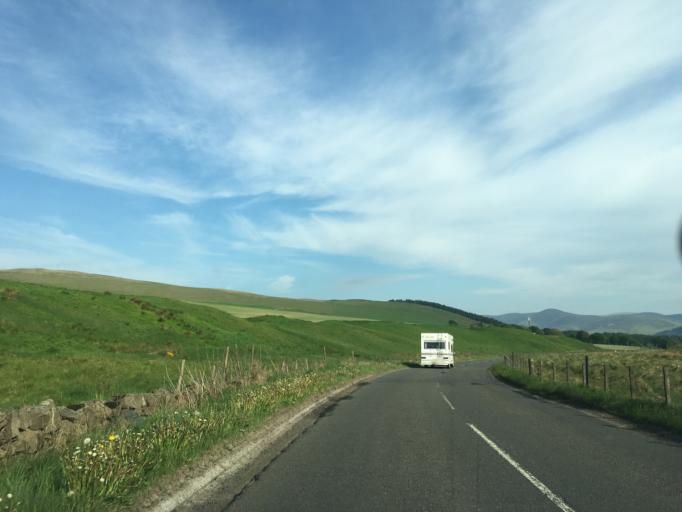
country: GB
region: Scotland
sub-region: South Lanarkshire
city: Biggar
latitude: 55.6350
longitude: -3.4232
